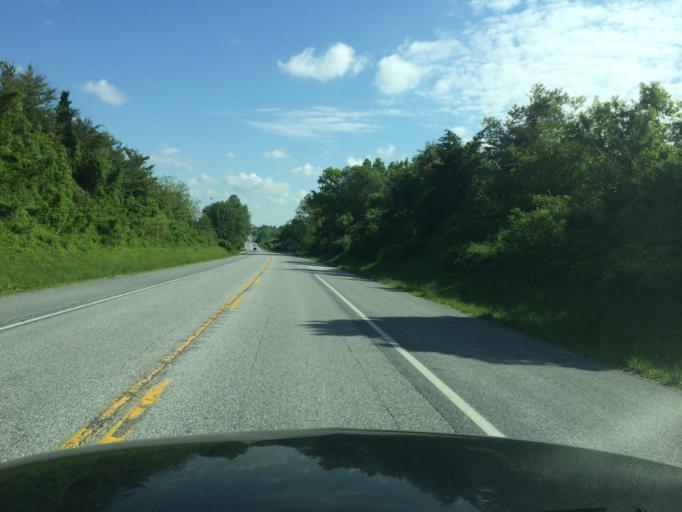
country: US
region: Maryland
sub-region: Carroll County
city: Westminster
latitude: 39.5472
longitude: -76.9863
